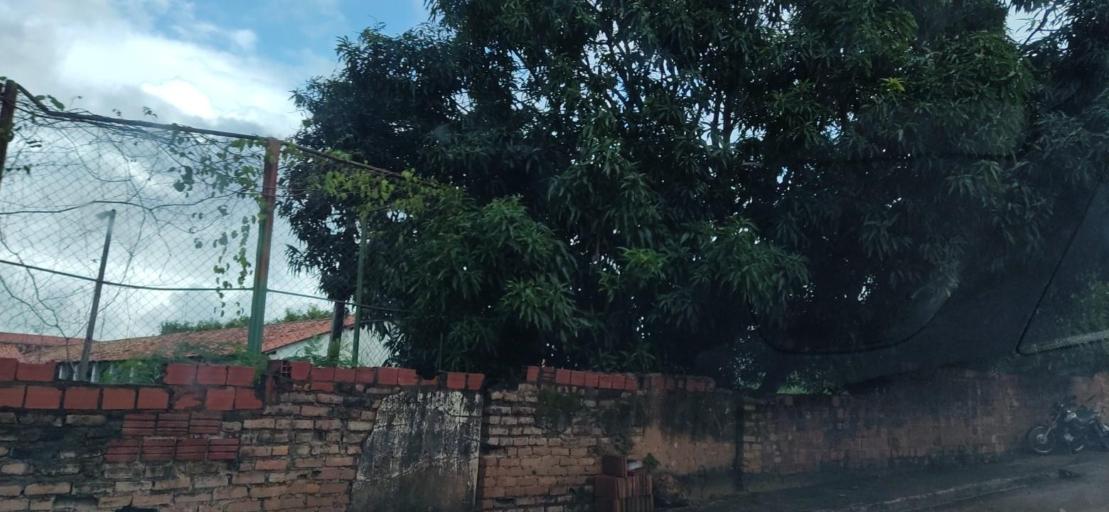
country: BR
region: Piaui
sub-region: Valenca Do Piaui
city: Valenca do Piaui
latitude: -6.1122
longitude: -41.7877
